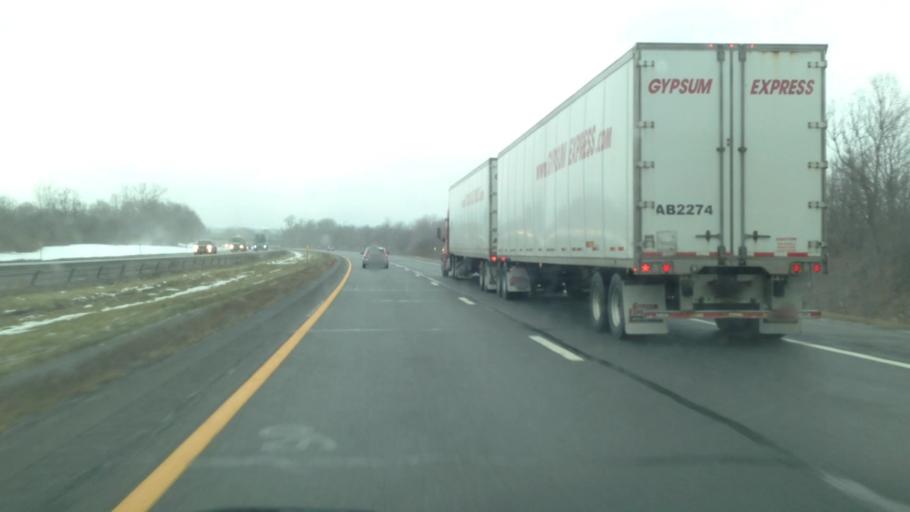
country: US
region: New York
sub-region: Montgomery County
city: Amsterdam
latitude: 42.9087
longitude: -74.1383
